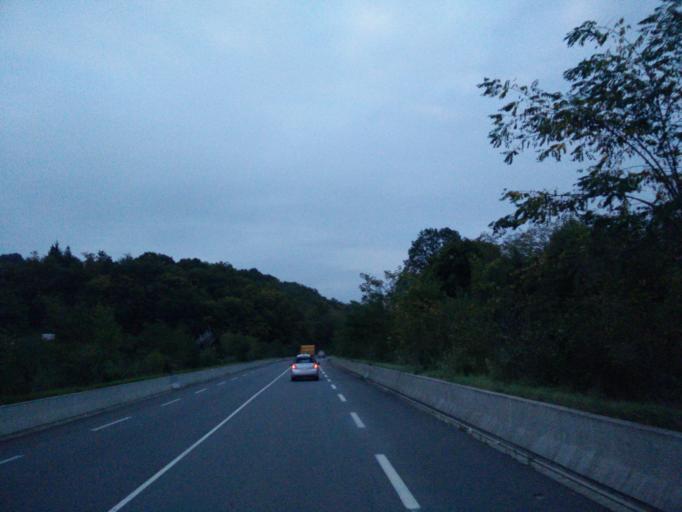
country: FR
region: Aquitaine
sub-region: Departement de la Dordogne
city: Sarlat-la-Caneda
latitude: 44.8933
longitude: 1.1994
